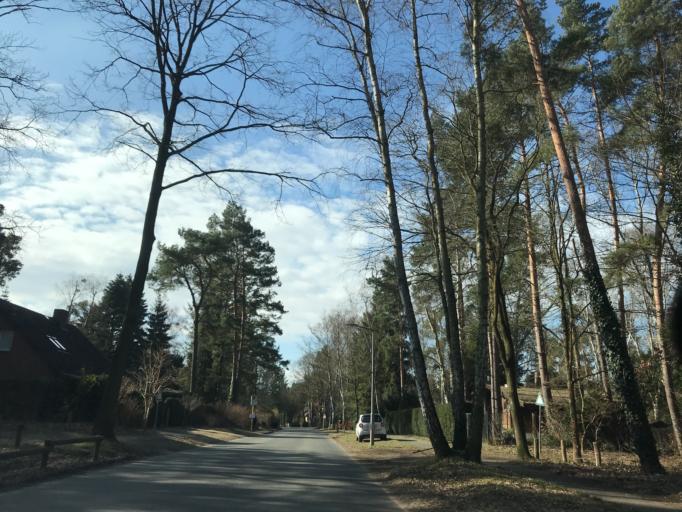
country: DE
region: Berlin
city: Kladow
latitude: 52.4575
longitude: 13.1240
